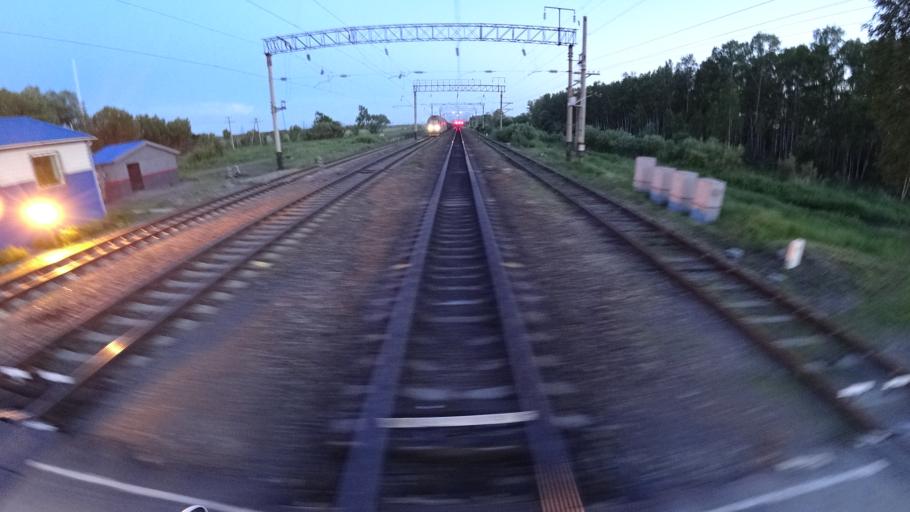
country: RU
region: Khabarovsk Krai
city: Khor
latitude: 47.8455
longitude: 134.9450
